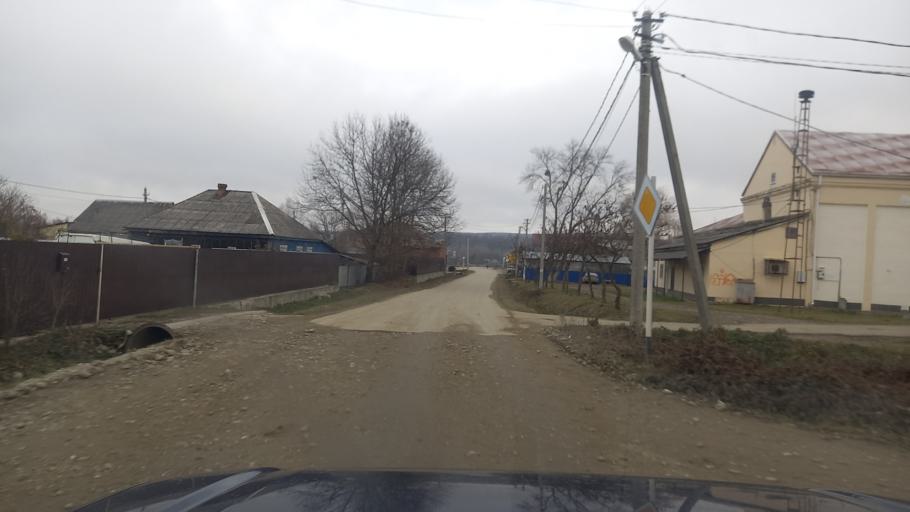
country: RU
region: Krasnodarskiy
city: Neftegorsk
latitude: 44.2480
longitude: 39.7635
